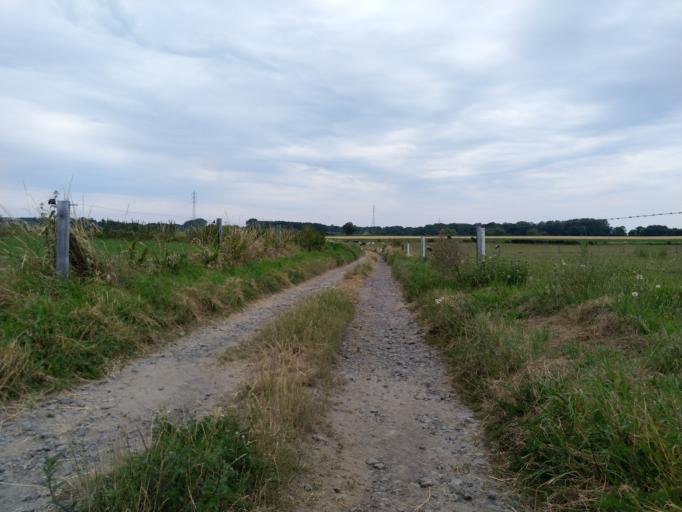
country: BE
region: Wallonia
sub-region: Province du Hainaut
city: Roeulx
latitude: 50.4909
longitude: 4.0527
